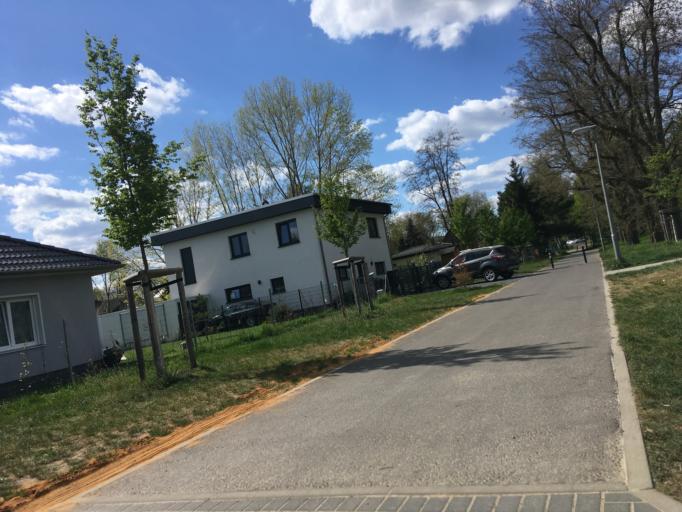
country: DE
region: Berlin
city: Mahlsdorf
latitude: 52.5168
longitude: 13.6228
